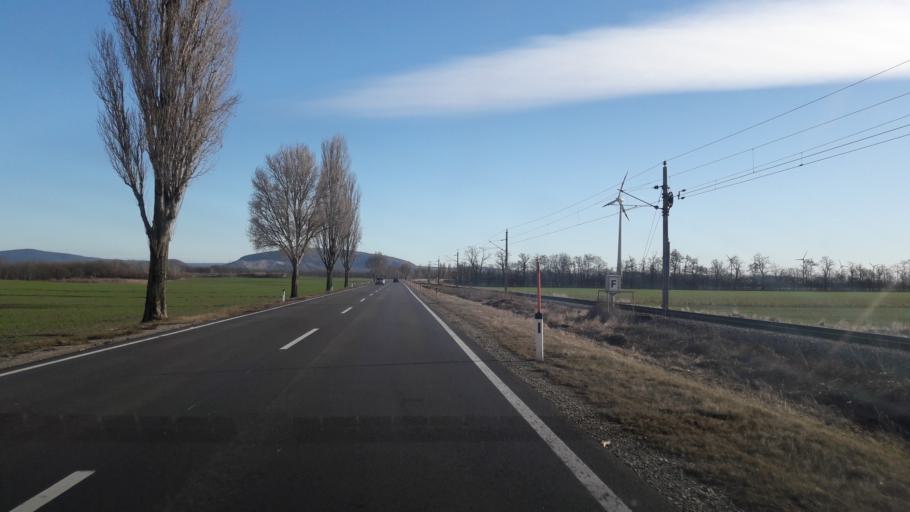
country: AT
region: Lower Austria
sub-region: Politischer Bezirk Bruck an der Leitha
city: Petronell-Carnuntum
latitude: 48.1113
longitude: 16.8262
